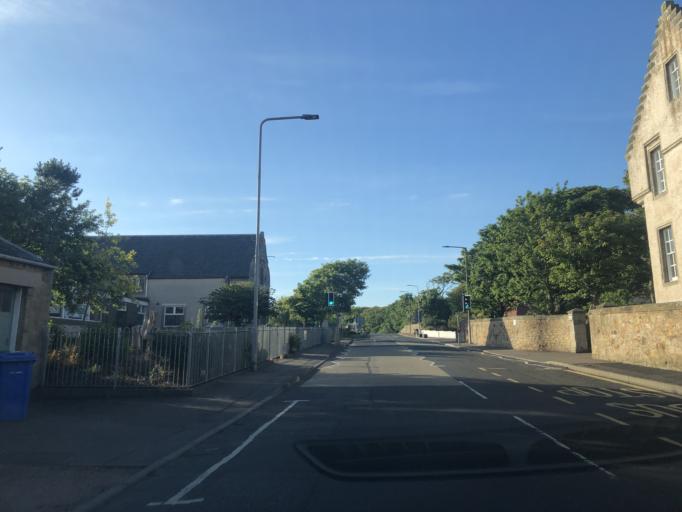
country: GB
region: Scotland
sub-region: Fife
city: Saint Monance
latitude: 56.1922
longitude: -2.8219
